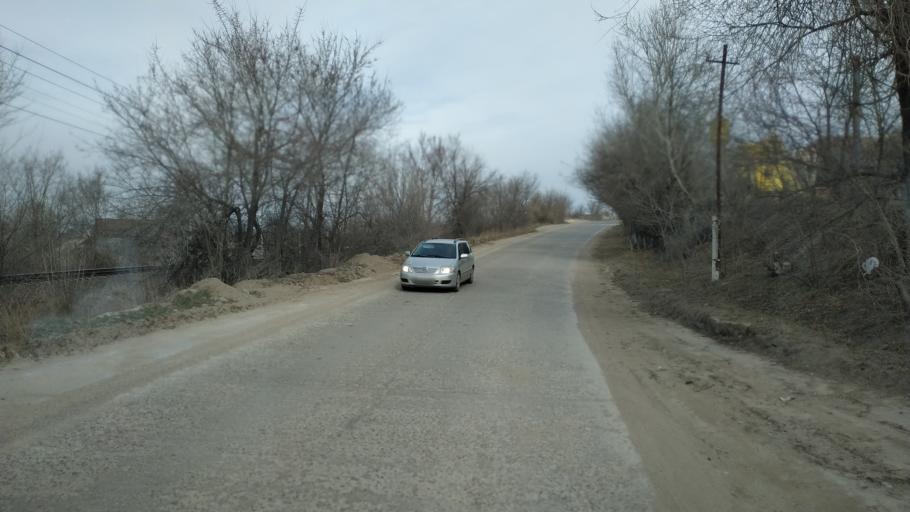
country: MD
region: Chisinau
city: Vatra
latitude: 47.0783
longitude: 28.7417
